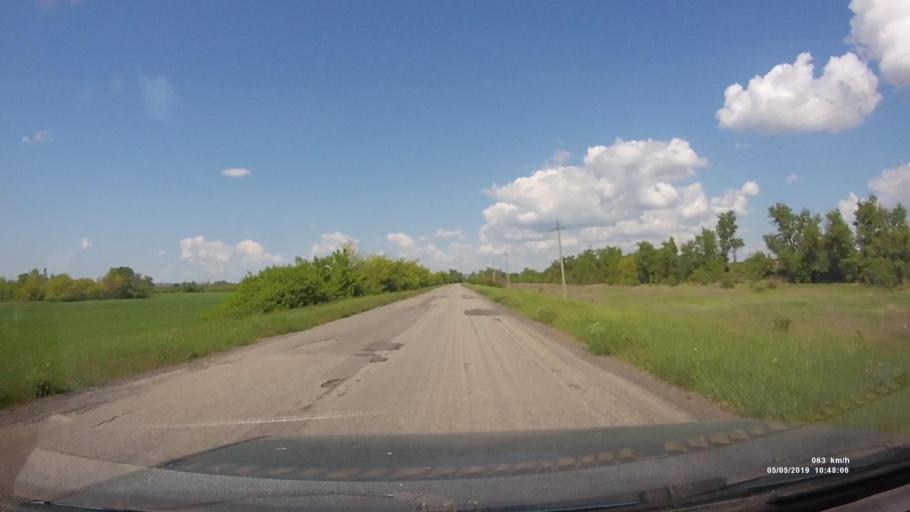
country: RU
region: Rostov
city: Ust'-Donetskiy
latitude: 47.6412
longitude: 40.8243
